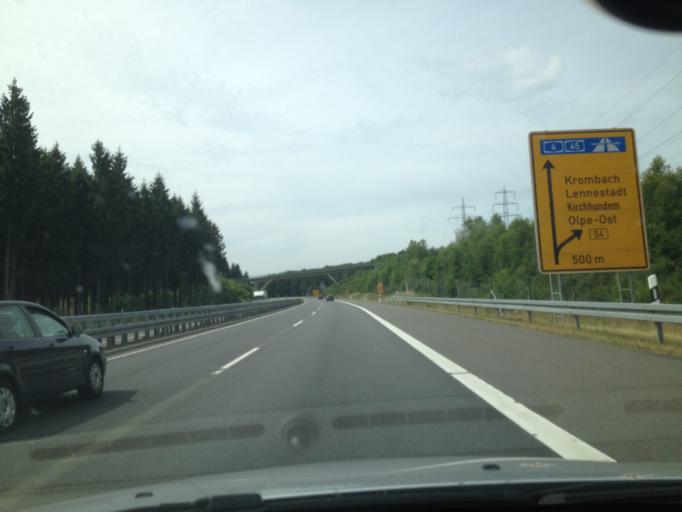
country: DE
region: North Rhine-Westphalia
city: Kreuztal
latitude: 50.9868
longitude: 7.9353
